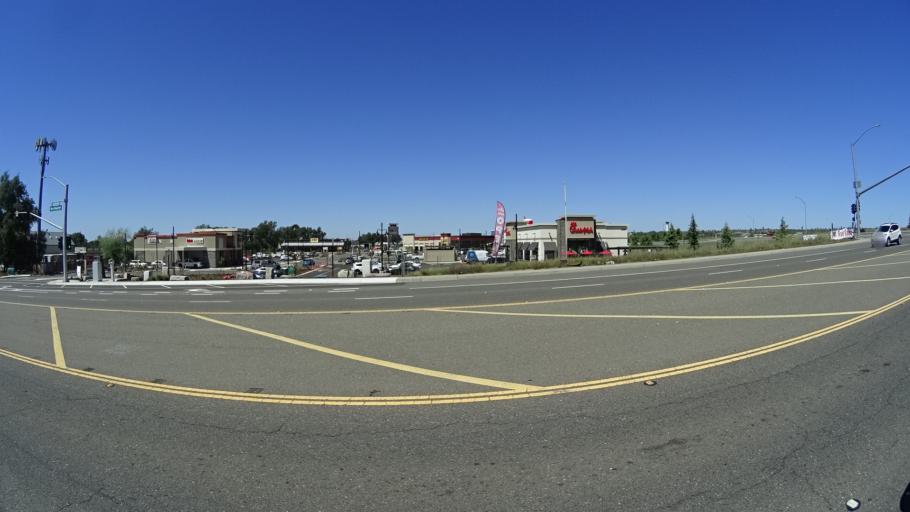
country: US
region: California
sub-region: Placer County
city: Loomis
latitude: 38.8000
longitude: -121.2054
